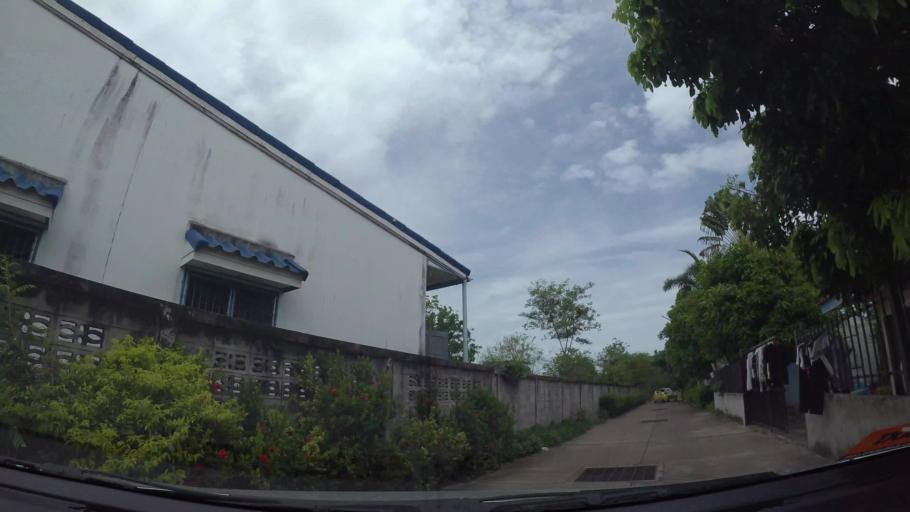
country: TH
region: Chon Buri
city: Sattahip
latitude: 12.6767
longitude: 100.9067
